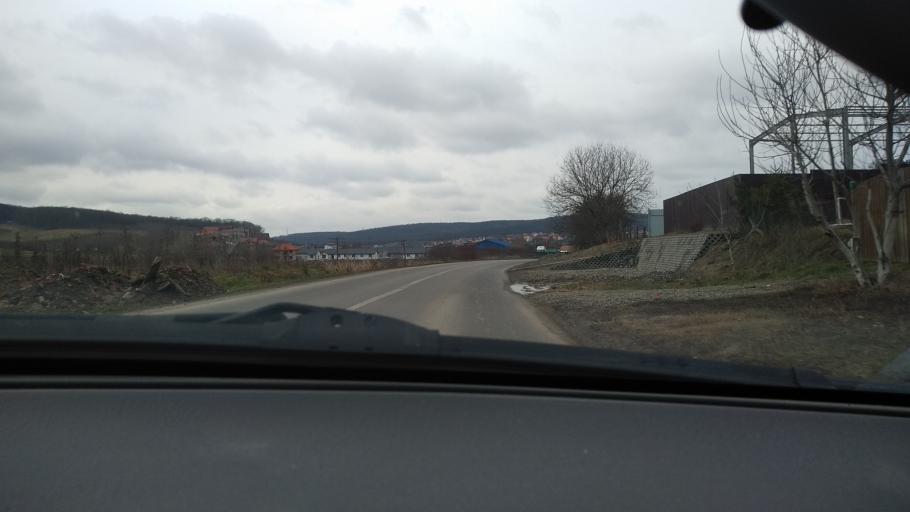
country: RO
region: Mures
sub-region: Comuna Livezeni
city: Livezeni
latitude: 46.5451
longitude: 24.6428
